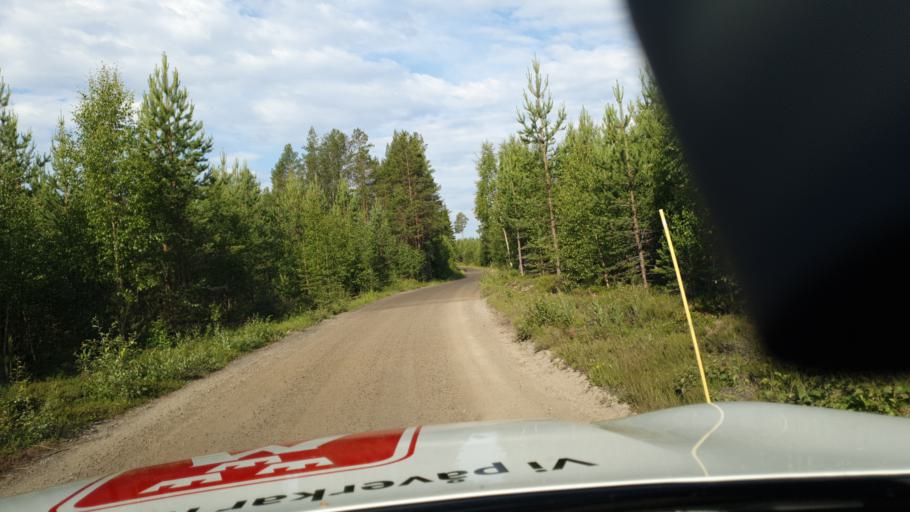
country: SE
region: Vaesterbotten
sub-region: Robertsfors Kommun
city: Robertsfors
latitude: 64.2281
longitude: 21.0523
